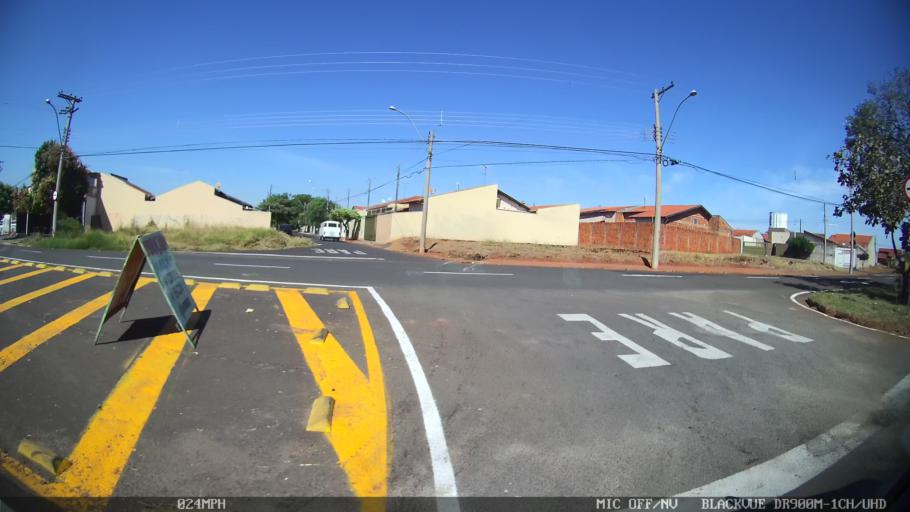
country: BR
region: Sao Paulo
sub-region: Sao Jose Do Rio Preto
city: Sao Jose do Rio Preto
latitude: -20.7653
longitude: -49.4032
